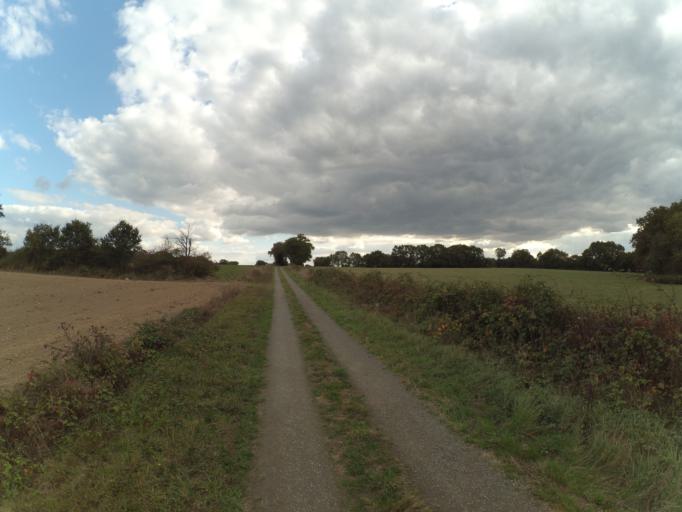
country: FR
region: Pays de la Loire
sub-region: Departement de la Loire-Atlantique
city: Remouille
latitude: 47.0694
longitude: -1.3703
